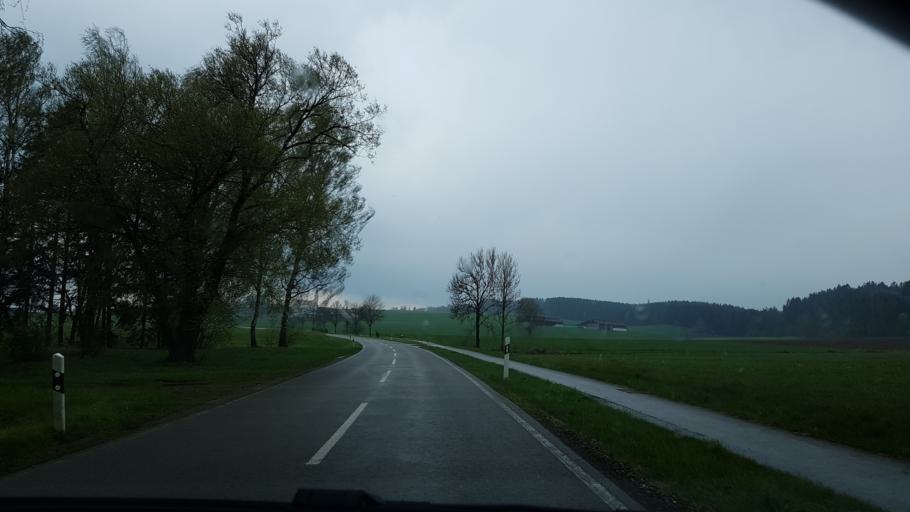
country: DE
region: Baden-Wuerttemberg
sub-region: Tuebingen Region
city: Wain
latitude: 48.2237
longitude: 10.0165
